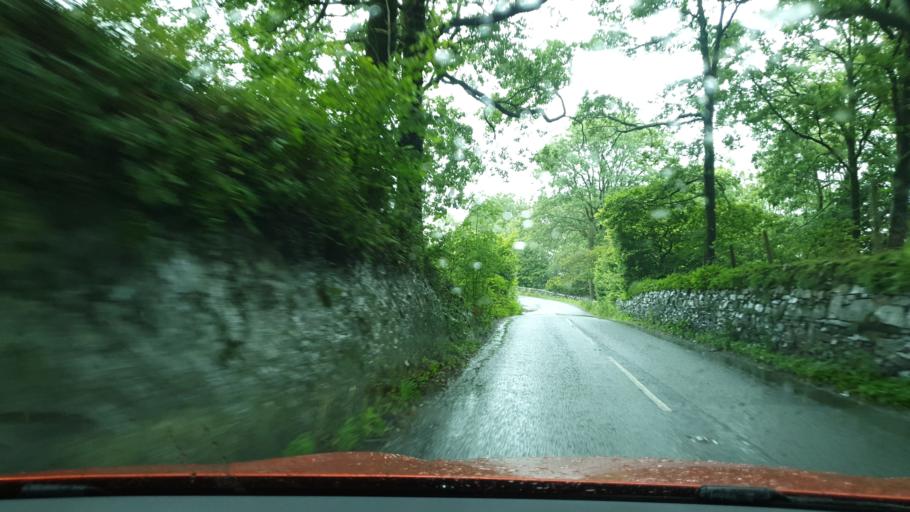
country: GB
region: England
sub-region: Cumbria
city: Ulverston
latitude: 54.3431
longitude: -3.0954
